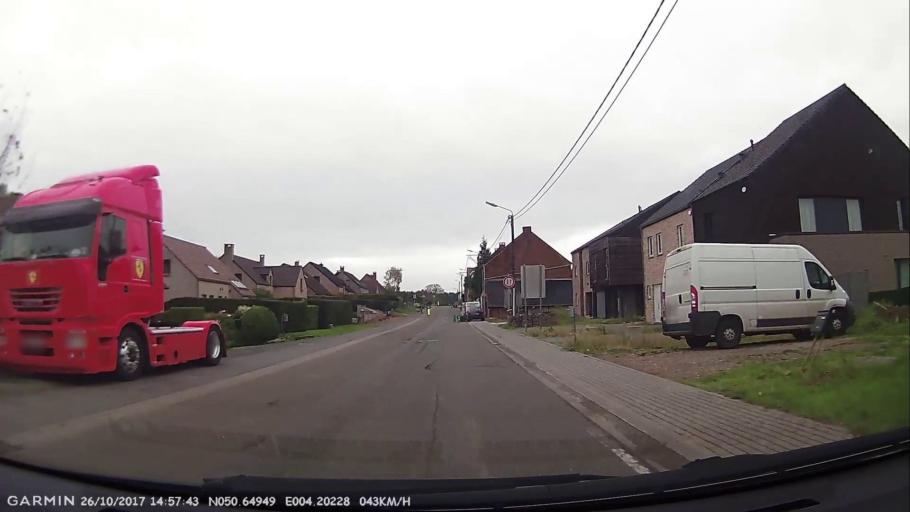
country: BE
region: Wallonia
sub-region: Province du Brabant Wallon
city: Tubize
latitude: 50.6495
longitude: 4.2023
